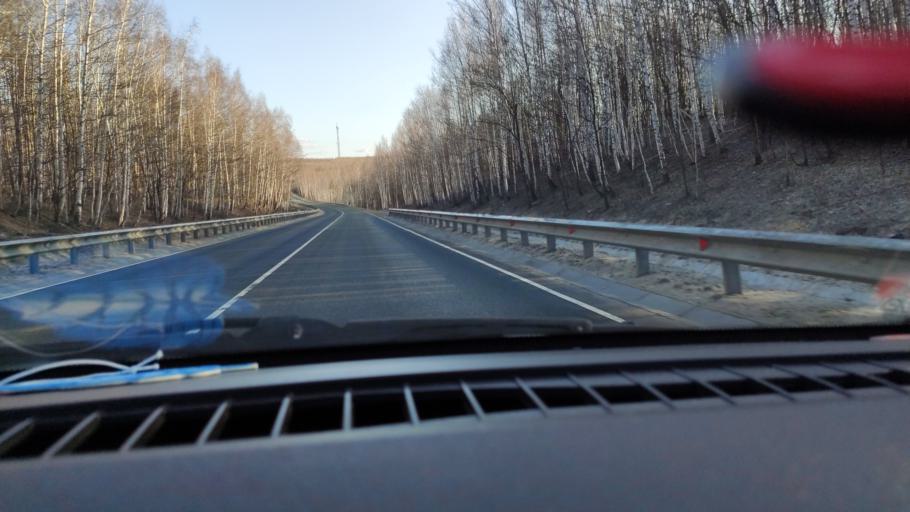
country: RU
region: Saratov
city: Khvalynsk
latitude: 52.4588
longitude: 48.0165
